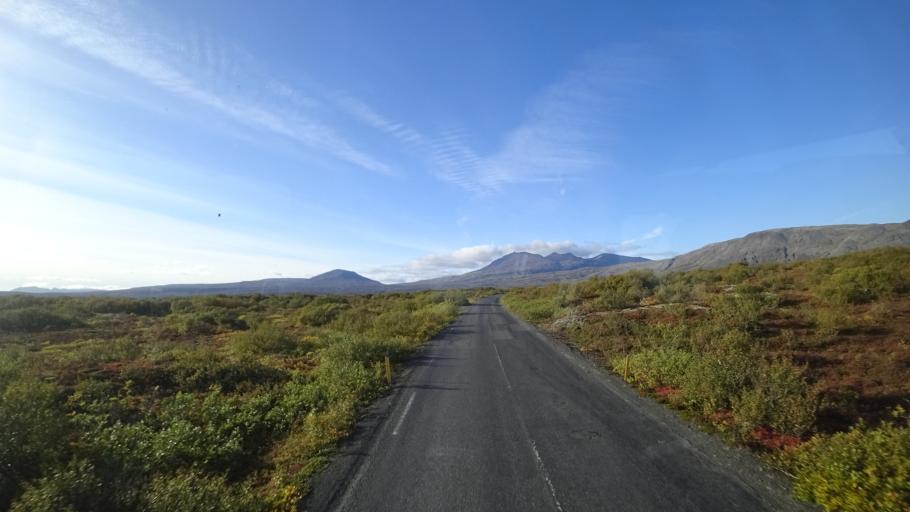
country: IS
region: South
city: Hveragerdi
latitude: 64.2670
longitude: -21.0617
